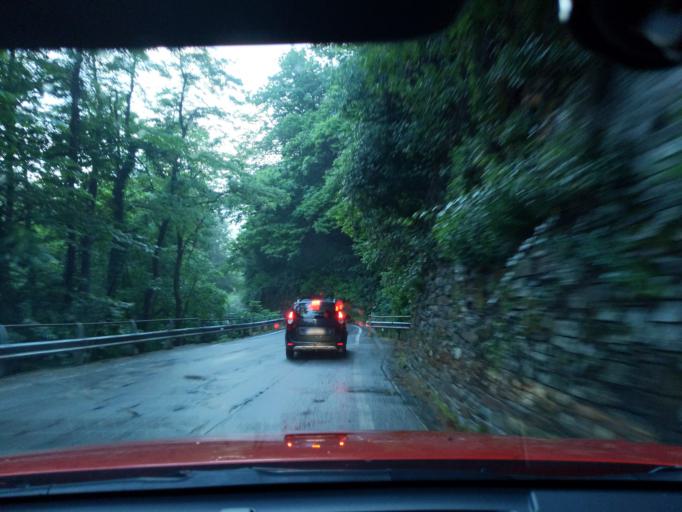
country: IT
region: Piedmont
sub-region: Provincia Verbano-Cusio-Ossola
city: Cavaglio-Spoccia
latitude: 46.0699
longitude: 8.6127
